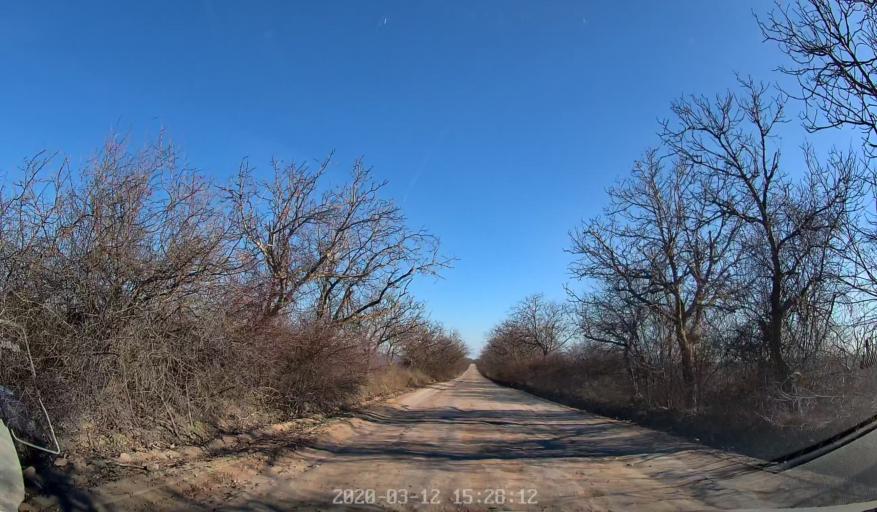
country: MD
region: Chisinau
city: Ciorescu
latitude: 47.1699
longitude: 28.9297
